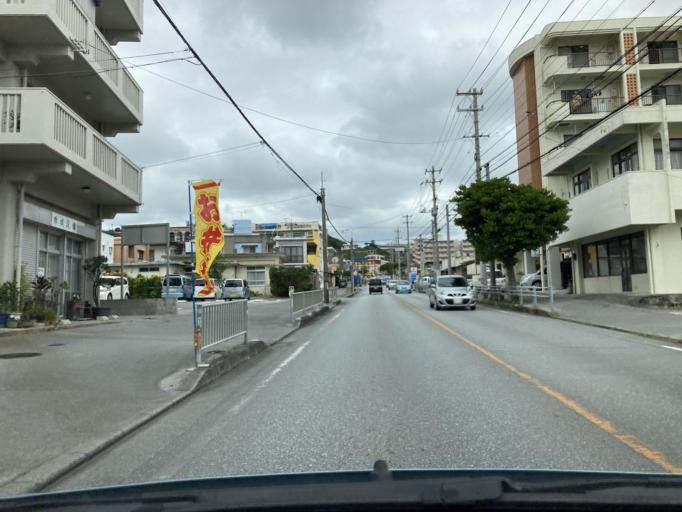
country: JP
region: Okinawa
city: Ginowan
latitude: 26.2307
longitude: 127.7533
